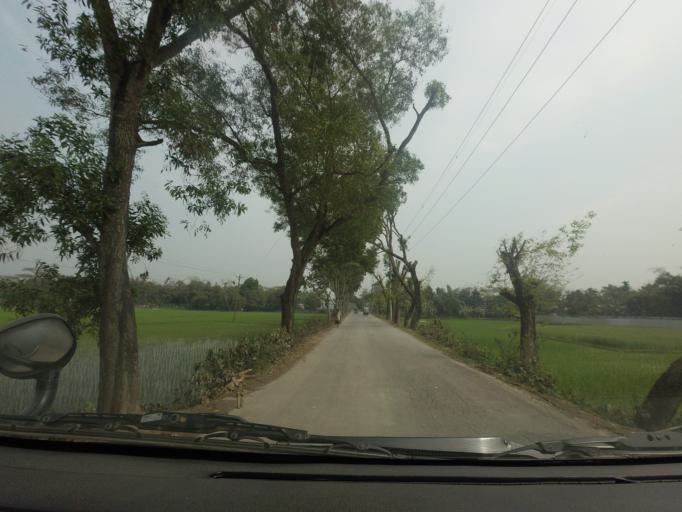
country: BD
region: Dhaka
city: Kishorganj
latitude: 24.3431
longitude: 90.7852
